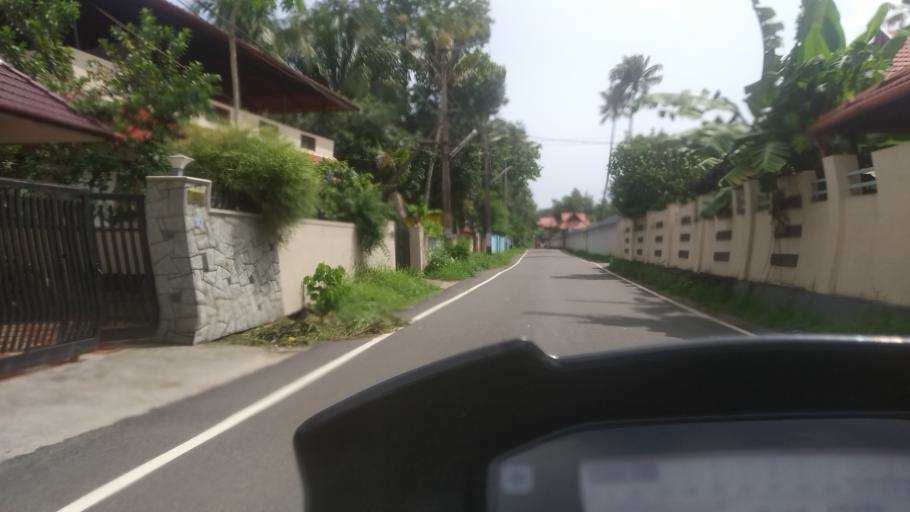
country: IN
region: Kerala
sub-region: Ernakulam
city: Elur
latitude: 10.1429
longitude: 76.2385
